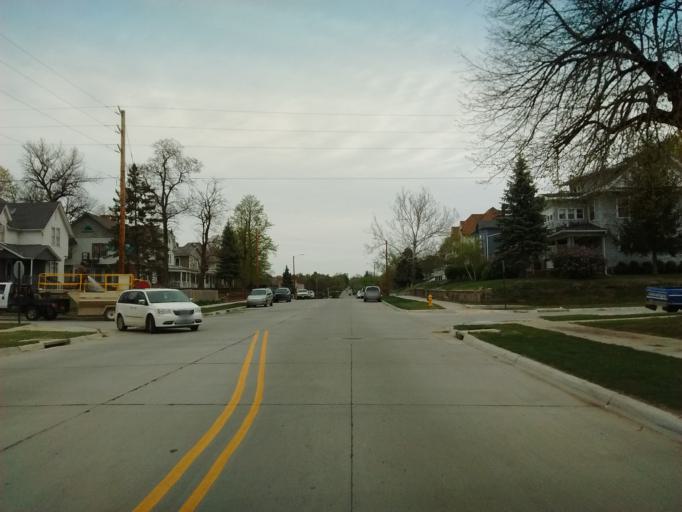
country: US
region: Iowa
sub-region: Woodbury County
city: Sioux City
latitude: 42.5058
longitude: -96.4020
